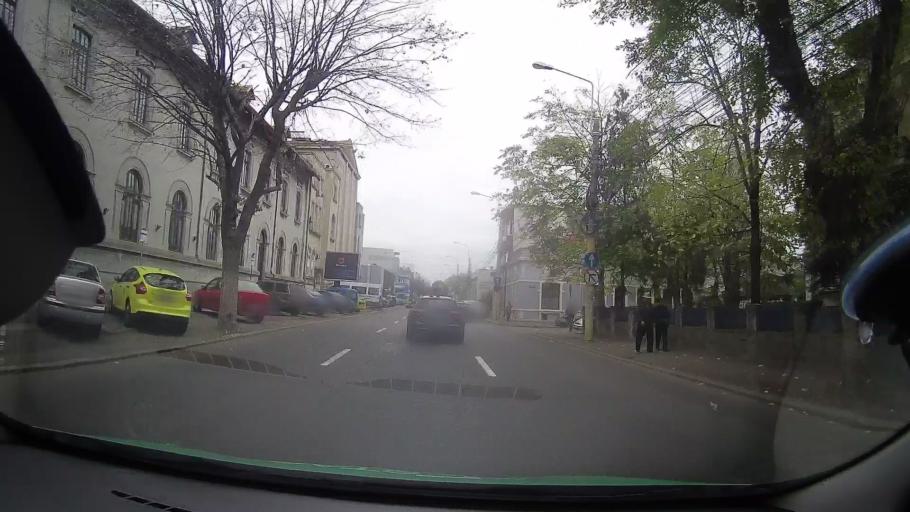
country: RO
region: Constanta
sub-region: Municipiul Constanta
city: Constanta
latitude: 44.1813
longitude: 28.6515
